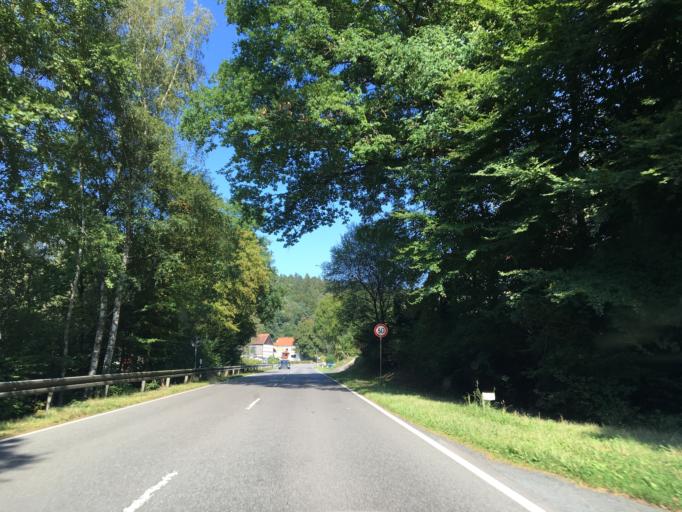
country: DE
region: Hesse
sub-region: Regierungsbezirk Giessen
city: Munchhausen
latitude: 51.0047
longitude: 8.7523
